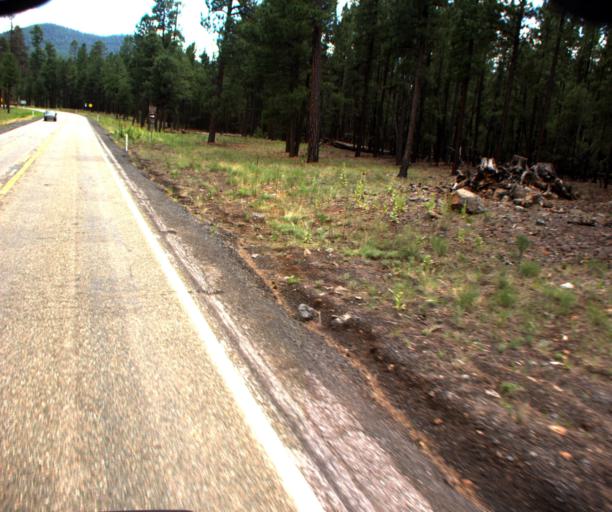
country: US
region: Arizona
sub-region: Coconino County
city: Flagstaff
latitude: 35.2726
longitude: -111.7436
